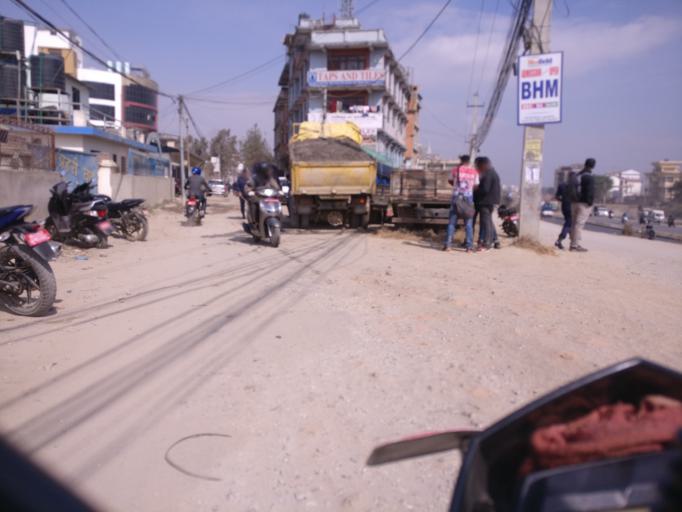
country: NP
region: Central Region
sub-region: Bagmati Zone
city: Patan
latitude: 27.6610
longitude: 85.3272
